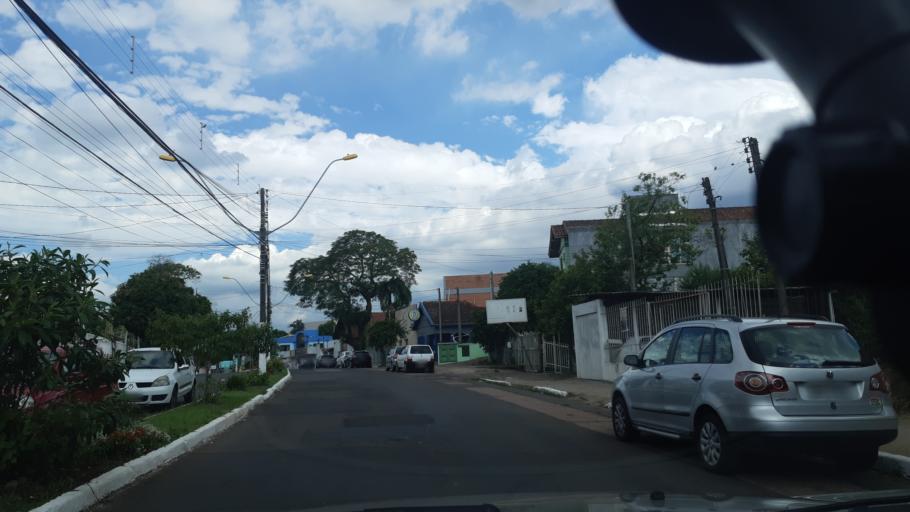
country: BR
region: Rio Grande do Sul
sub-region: Esteio
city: Esteio
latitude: -29.8491
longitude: -51.1674
